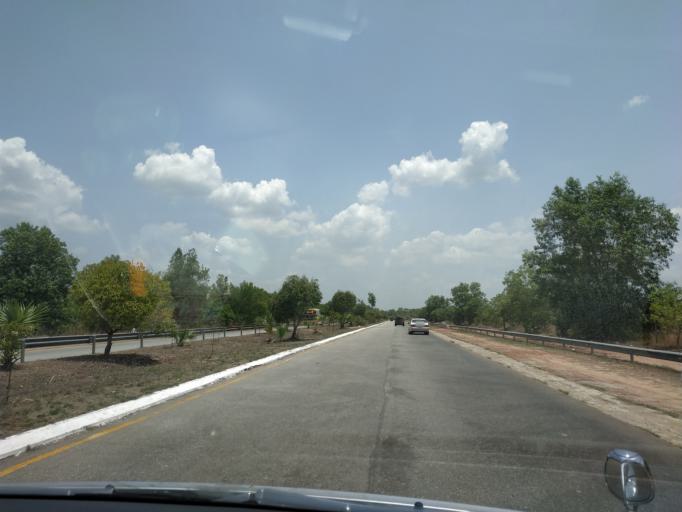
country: MM
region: Bago
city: Thanatpin
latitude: 17.2065
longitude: 96.1933
